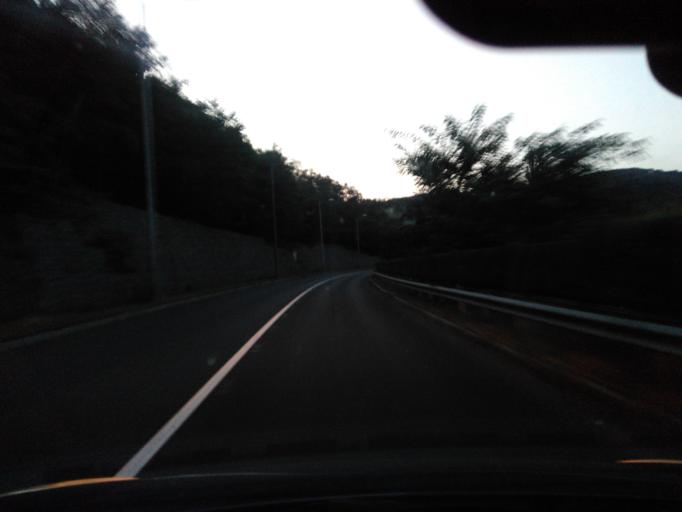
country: HU
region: Nograd
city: Salgotarjan
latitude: 48.1203
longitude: 19.8040
